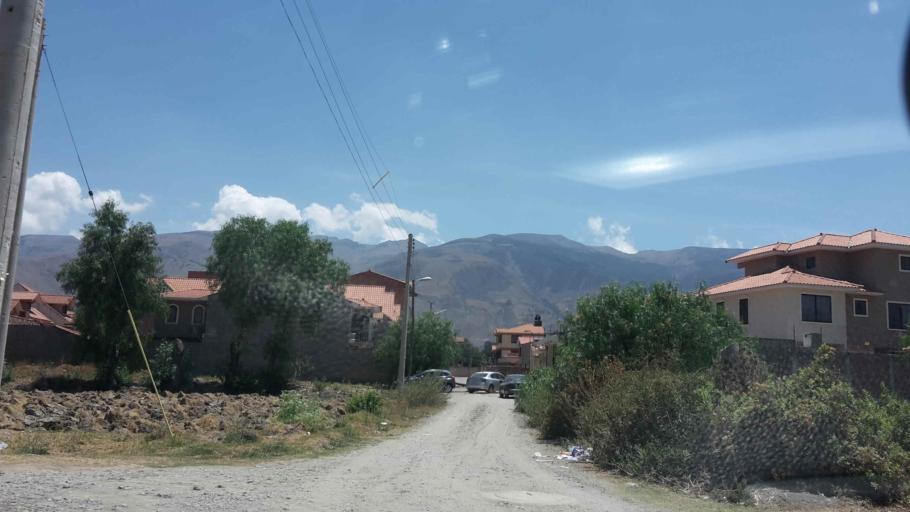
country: BO
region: Cochabamba
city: Cochabamba
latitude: -17.3700
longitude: -66.1933
